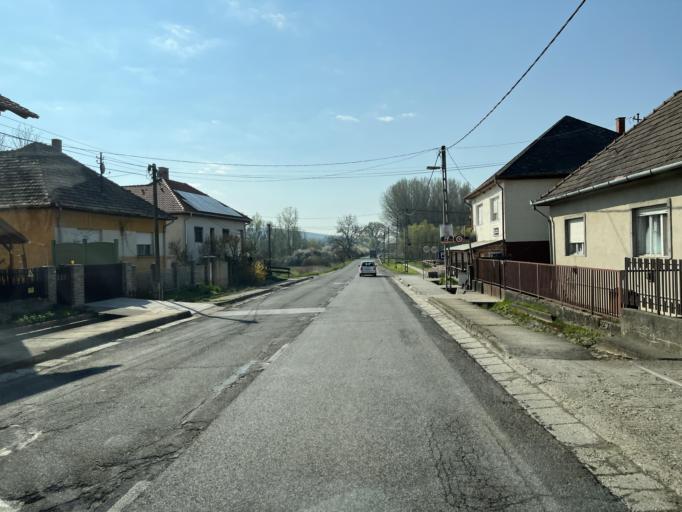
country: HU
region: Pest
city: Galgamacsa
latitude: 47.6984
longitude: 19.3992
